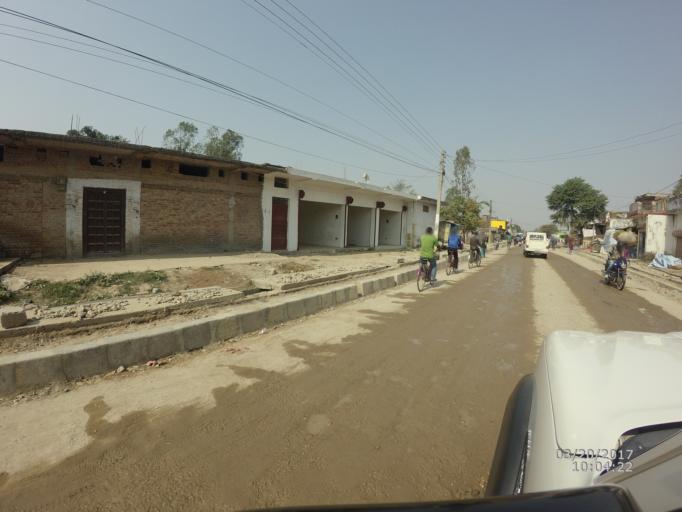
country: NP
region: Mid Western
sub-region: Bheri Zone
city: Nepalgunj
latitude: 28.1003
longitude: 81.6559
